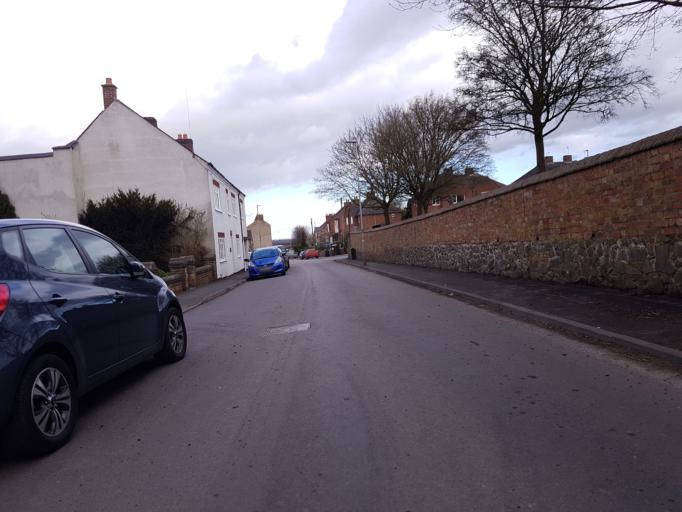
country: GB
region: England
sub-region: Leicestershire
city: Earl Shilton
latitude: 52.5800
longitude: -1.3061
